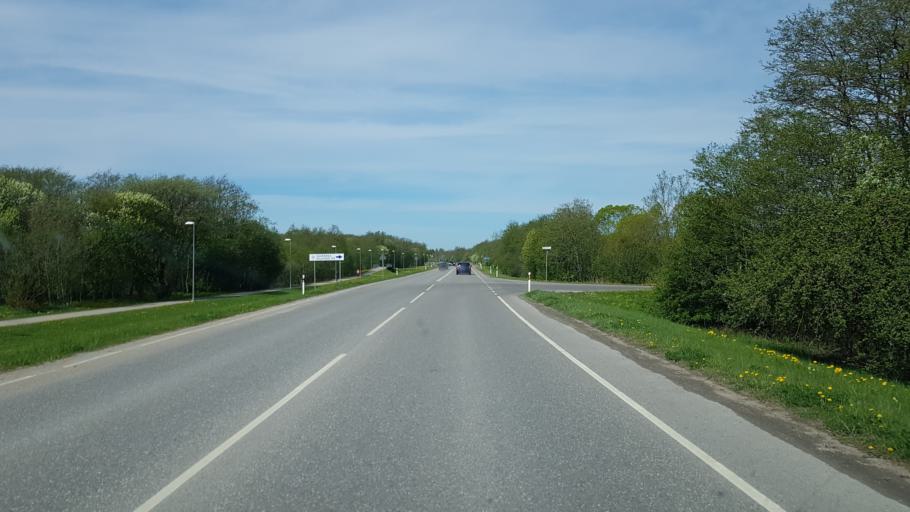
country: EE
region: Saare
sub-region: Kuressaare linn
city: Kuressaare
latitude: 58.2687
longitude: 22.4854
